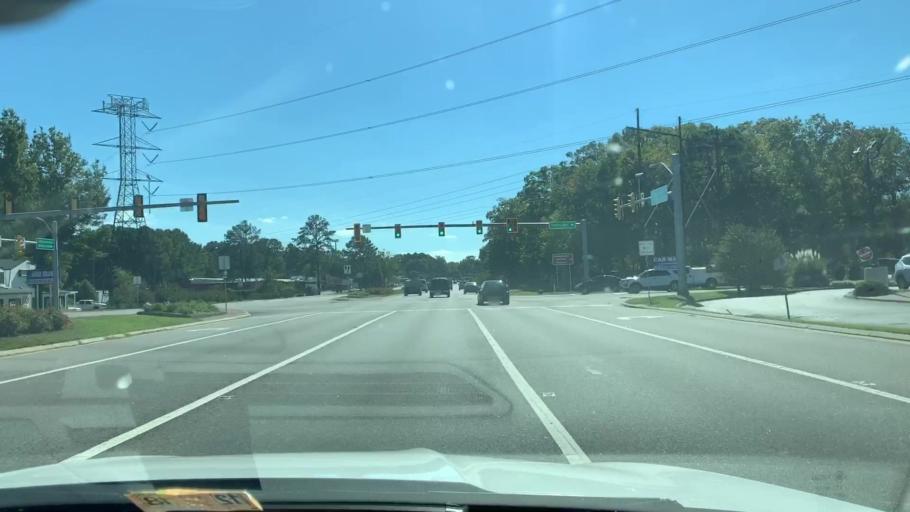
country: US
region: Virginia
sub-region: York County
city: Yorktown
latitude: 37.1458
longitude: -76.4585
